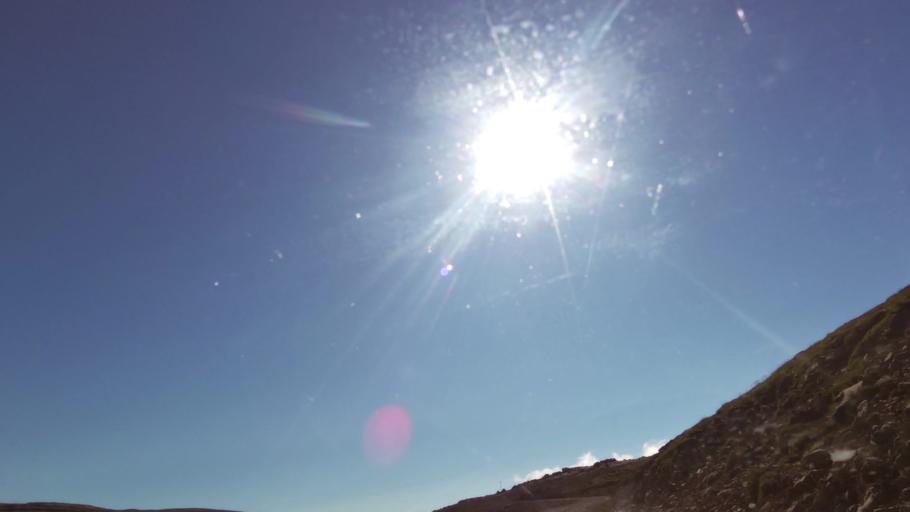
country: IS
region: West
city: Olafsvik
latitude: 65.5542
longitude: -24.1994
